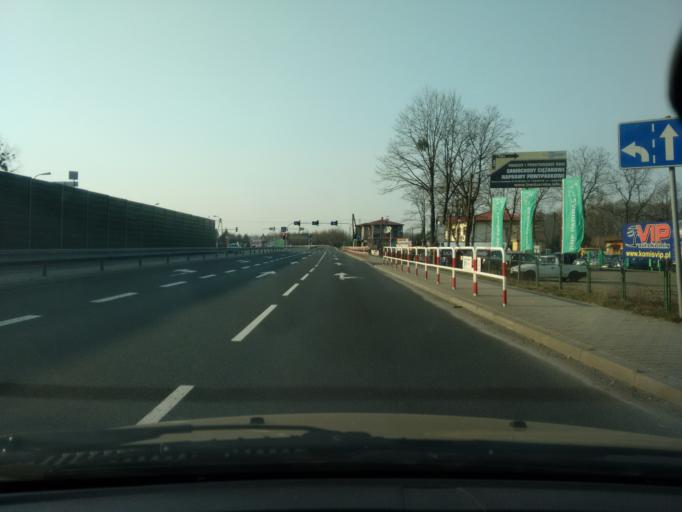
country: PL
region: Silesian Voivodeship
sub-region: Powiat cieszynski
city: Ochaby
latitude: 49.8414
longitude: 18.7699
